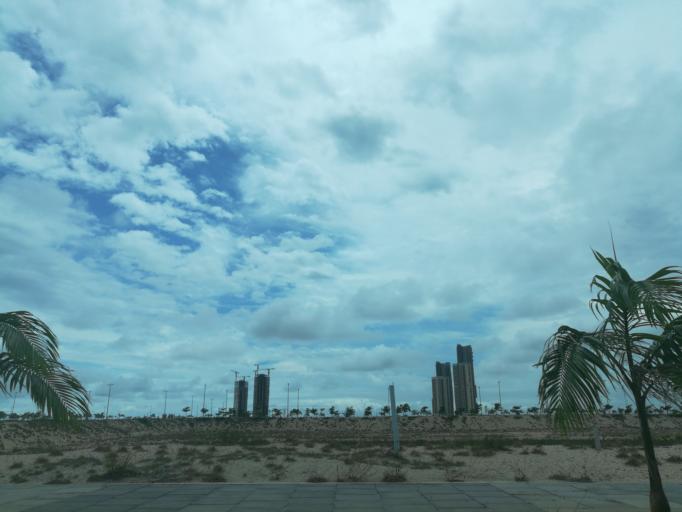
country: NG
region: Lagos
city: Ikoyi
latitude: 6.4108
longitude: 3.4195
